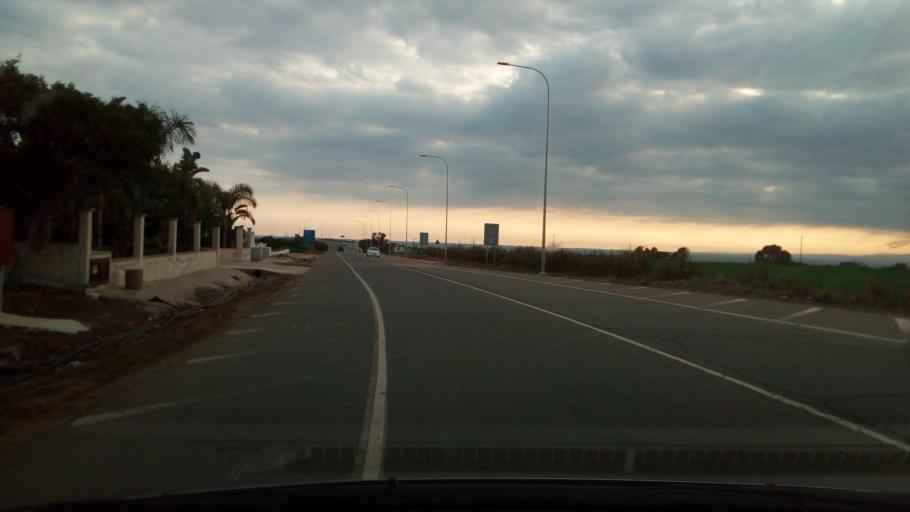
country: CY
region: Ammochostos
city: Avgorou
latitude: 34.9758
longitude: 33.8315
